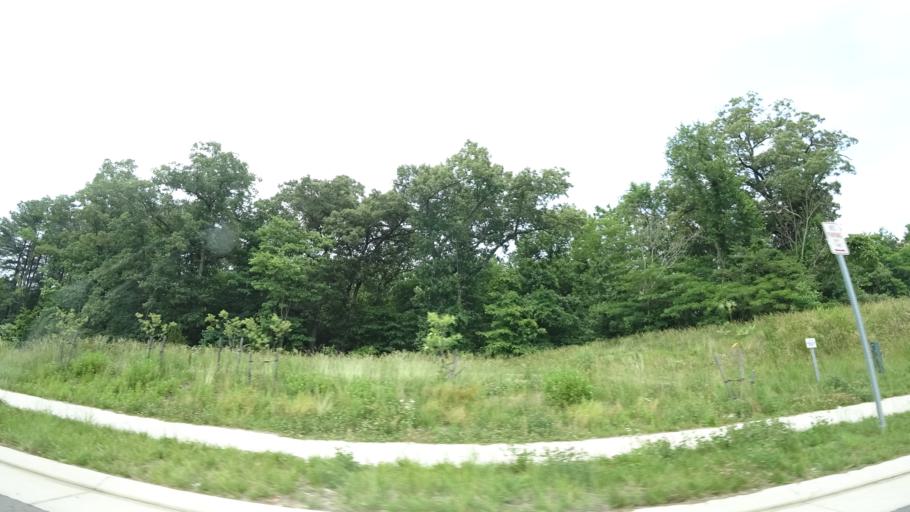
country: US
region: Virginia
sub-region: Fairfax County
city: Lorton
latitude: 38.7050
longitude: -77.2306
